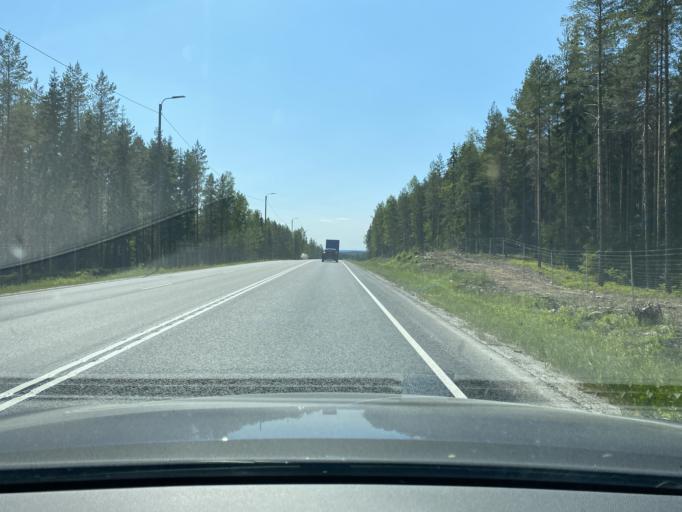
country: FI
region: Pirkanmaa
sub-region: Lounais-Pirkanmaa
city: Mouhijaervi
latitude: 61.3751
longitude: 23.1469
